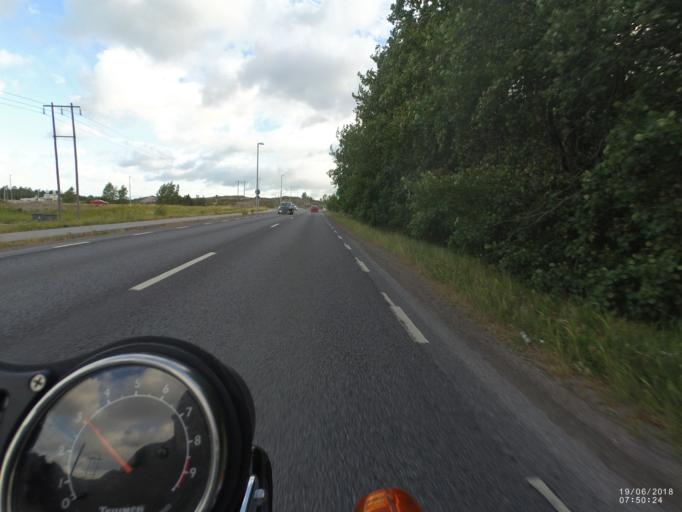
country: SE
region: Soedermanland
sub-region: Nykopings Kommun
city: Nykoping
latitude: 58.7702
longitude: 17.0271
